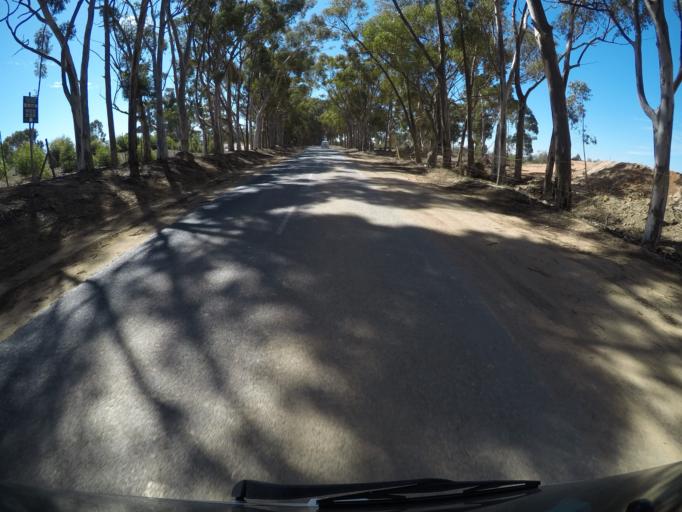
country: ZA
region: Western Cape
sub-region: City of Cape Town
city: Sunset Beach
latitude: -33.7597
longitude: 18.5535
